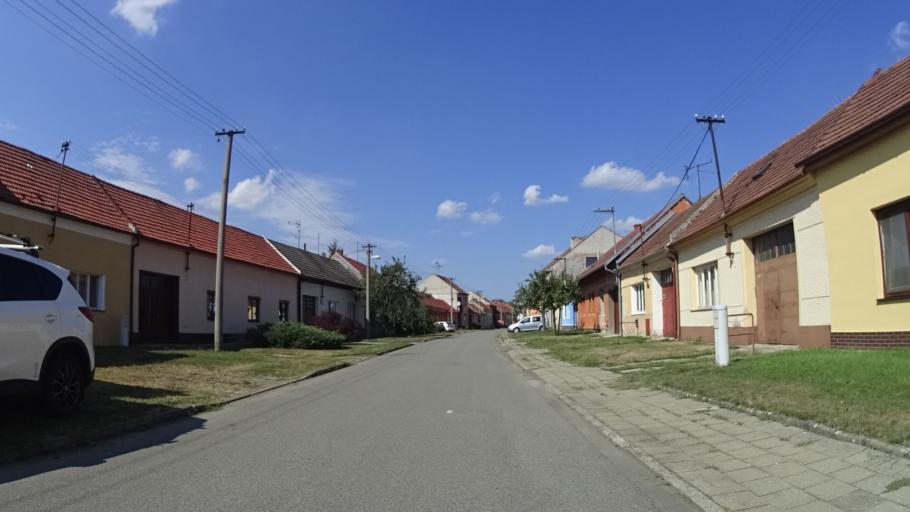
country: CZ
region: Zlin
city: Uhersky Ostroh
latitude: 48.9913
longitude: 17.4005
